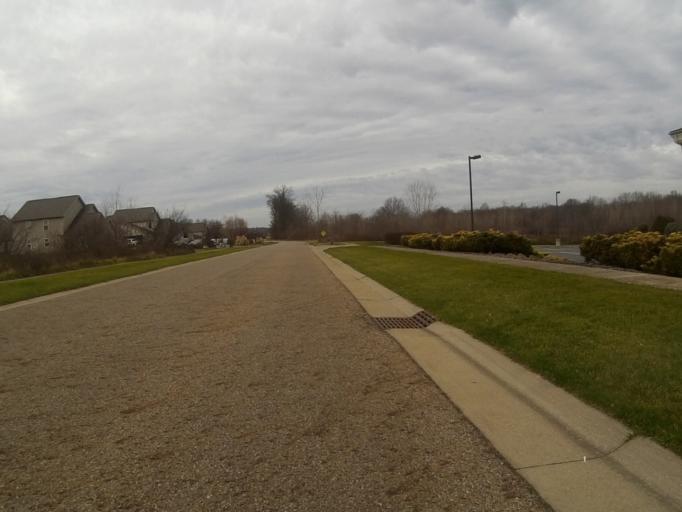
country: US
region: Ohio
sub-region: Portage County
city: Brimfield
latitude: 41.1110
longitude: -81.3494
